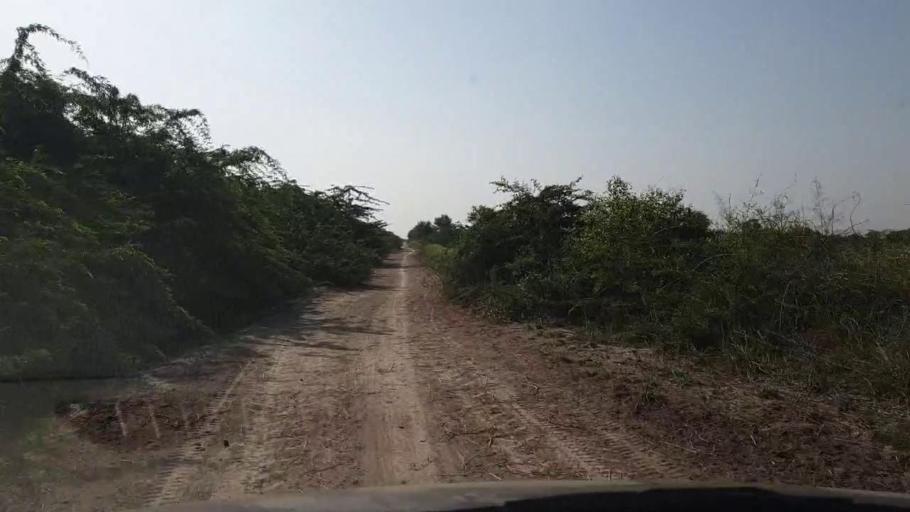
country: PK
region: Sindh
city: Kadhan
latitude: 24.6008
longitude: 69.0747
